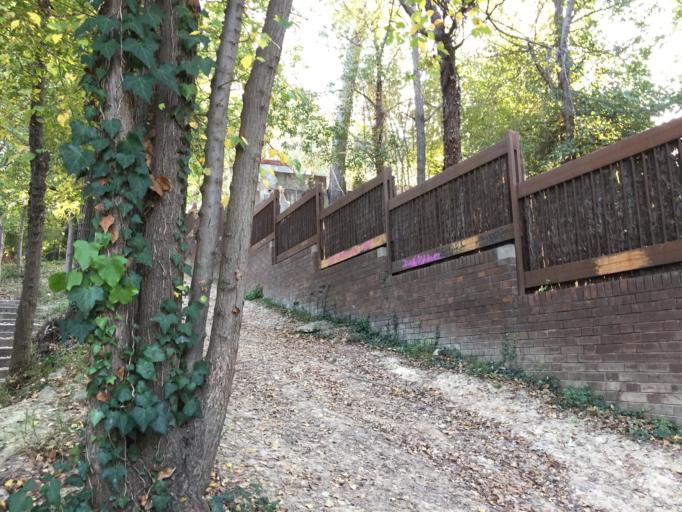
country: ES
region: Catalonia
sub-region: Provincia de Barcelona
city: Sants-Montjuic
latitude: 41.3678
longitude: 2.1610
